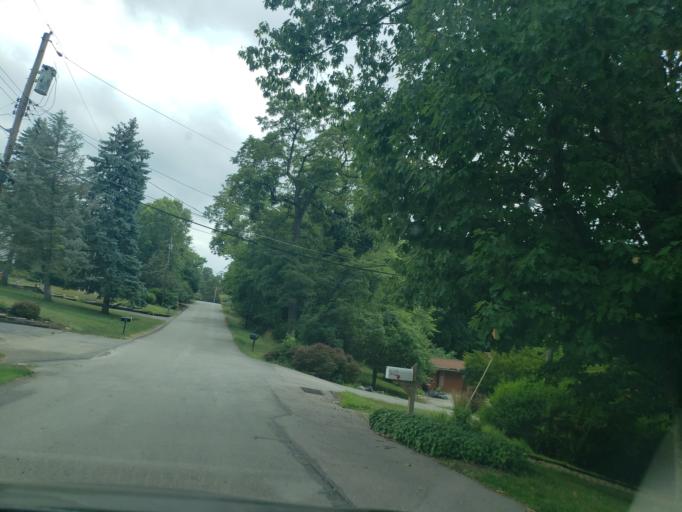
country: US
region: Pennsylvania
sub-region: Allegheny County
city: Coraopolis
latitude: 40.5402
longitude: -80.1609
